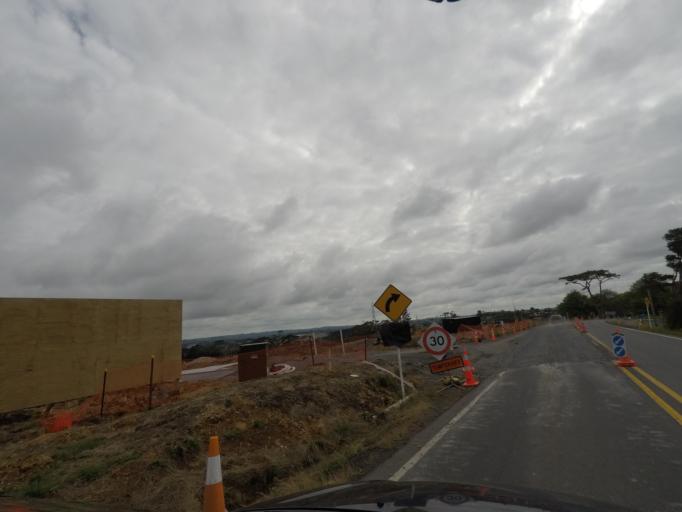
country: NZ
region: Auckland
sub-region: Auckland
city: Rosebank
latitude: -36.8361
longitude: 174.5946
